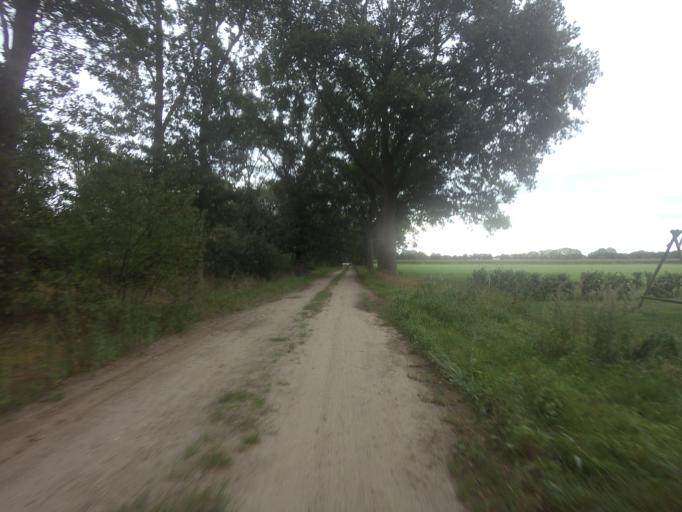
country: NL
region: Overijssel
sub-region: Gemeente Raalte
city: Raalte
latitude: 52.3142
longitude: 6.2968
